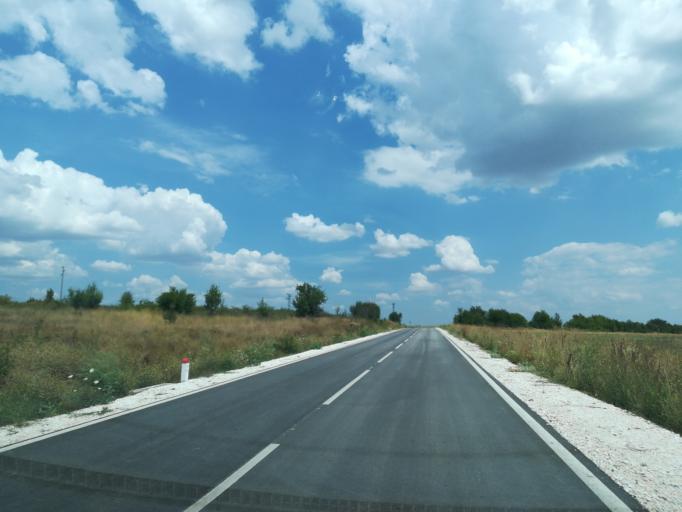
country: BG
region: Khaskovo
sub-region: Obshtina Mineralni Bani
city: Mineralni Bani
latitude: 41.9916
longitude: 25.1840
